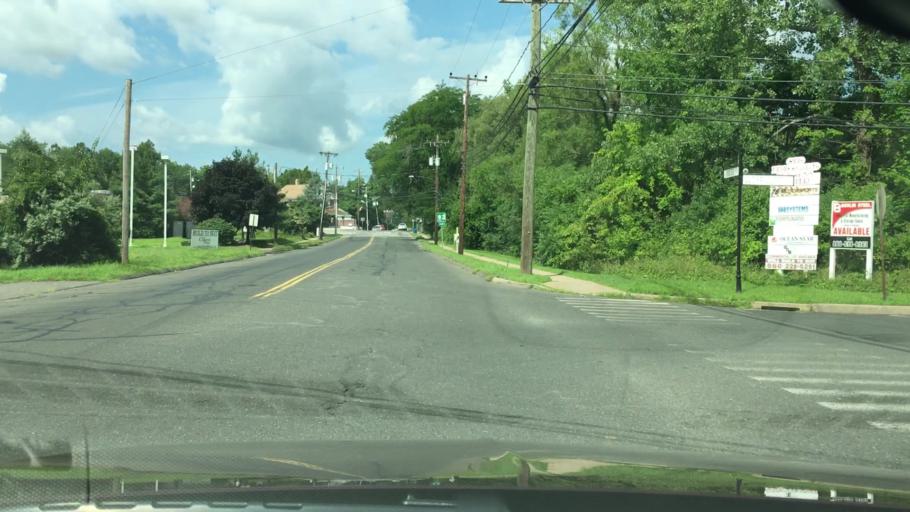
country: US
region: Connecticut
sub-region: Hartford County
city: Kensington
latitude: 41.6318
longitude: -72.7589
